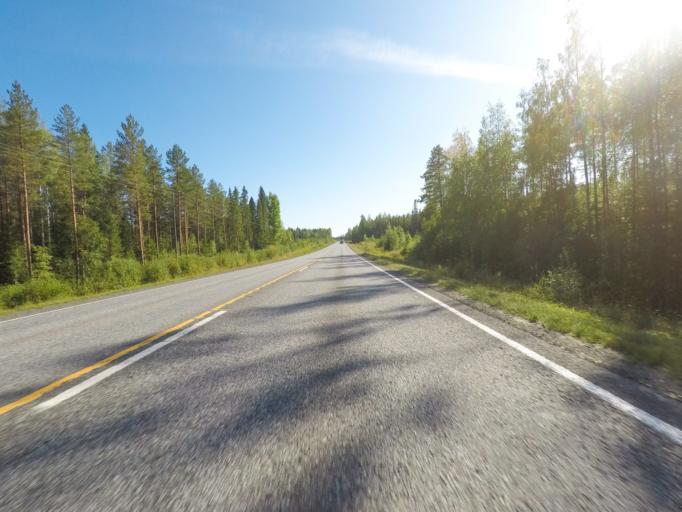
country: FI
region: Southern Savonia
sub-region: Pieksaemaeki
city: Juva
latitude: 61.9442
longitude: 27.8054
